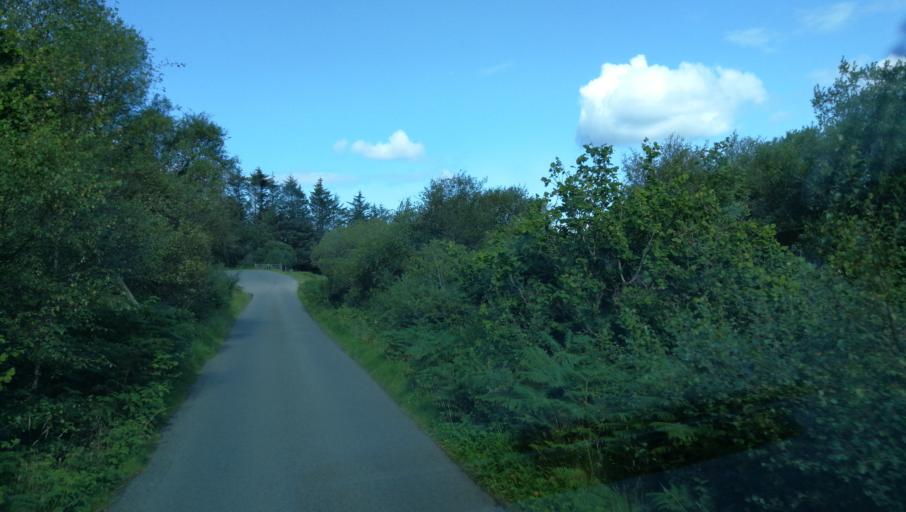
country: GB
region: Scotland
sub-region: Highland
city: Isle of Skye
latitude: 57.4467
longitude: -6.6455
